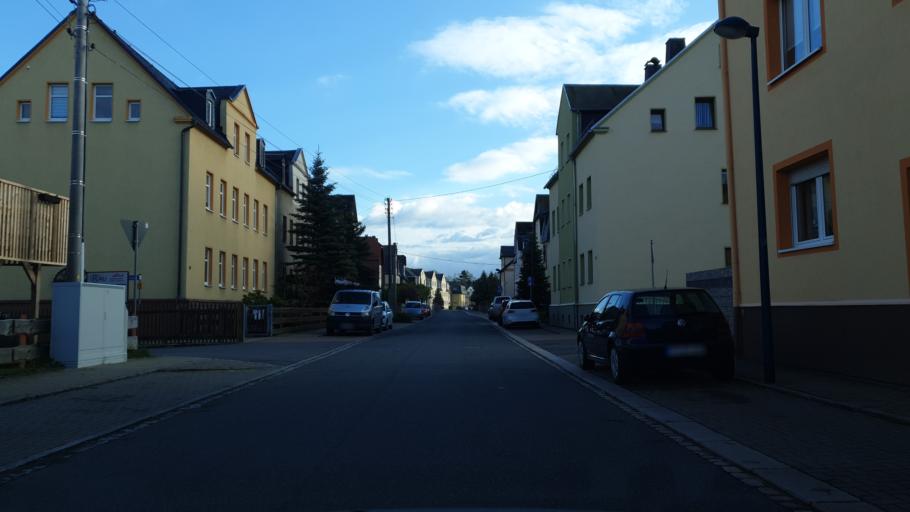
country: DE
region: Saxony
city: Lugau
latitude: 50.7253
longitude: 12.7384
